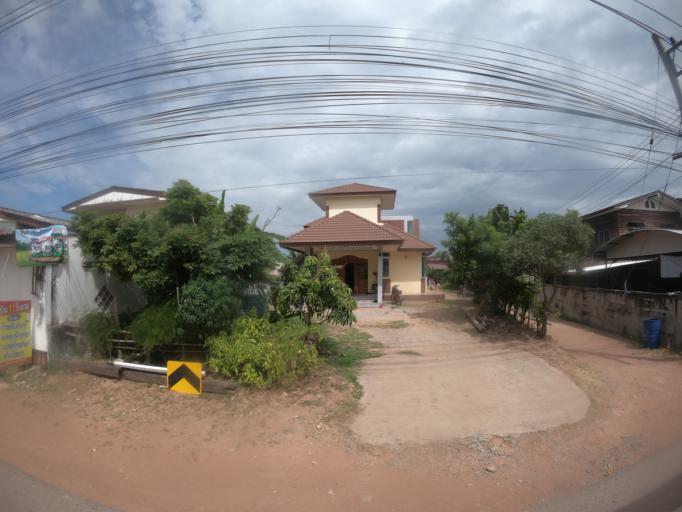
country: TH
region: Maha Sarakham
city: Chiang Yuen
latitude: 16.3442
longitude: 103.1481
